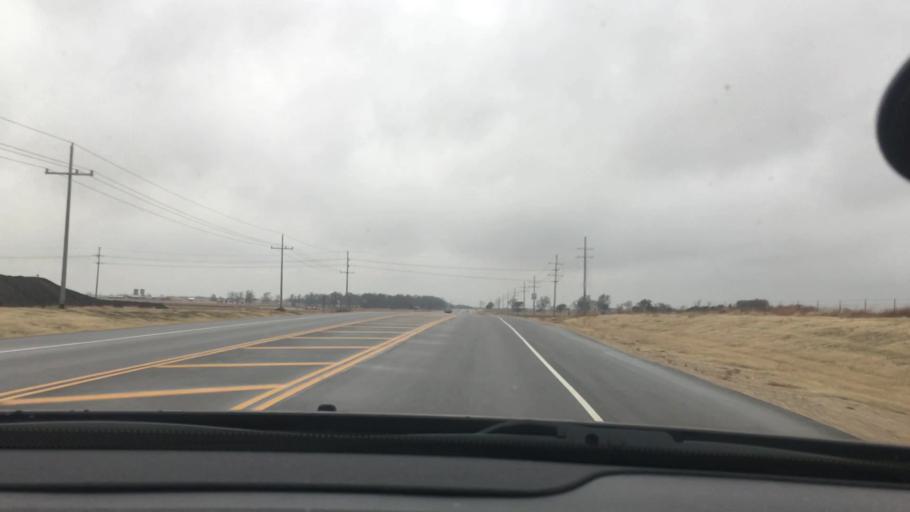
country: US
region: Oklahoma
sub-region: Johnston County
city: Tishomingo
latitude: 34.3627
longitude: -96.6358
